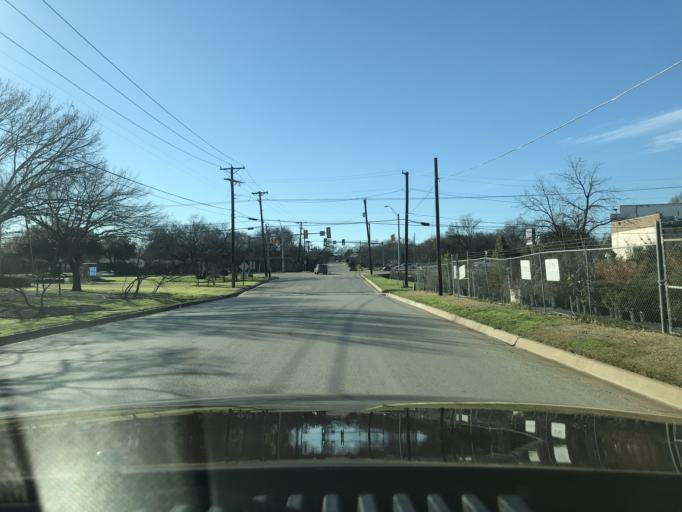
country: US
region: Texas
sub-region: Tarrant County
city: Edgecliff Village
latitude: 32.6614
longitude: -97.3475
